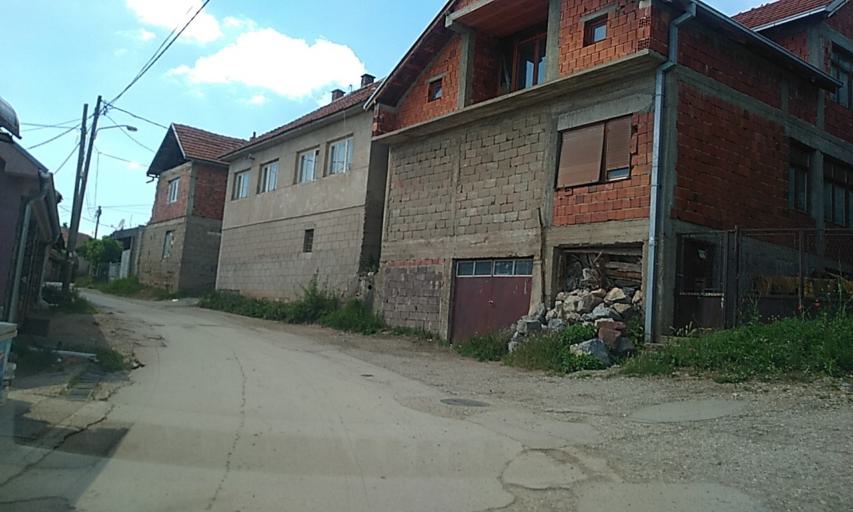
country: RS
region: Central Serbia
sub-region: Nisavski Okrug
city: Niska Banja
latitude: 43.3651
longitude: 22.0032
